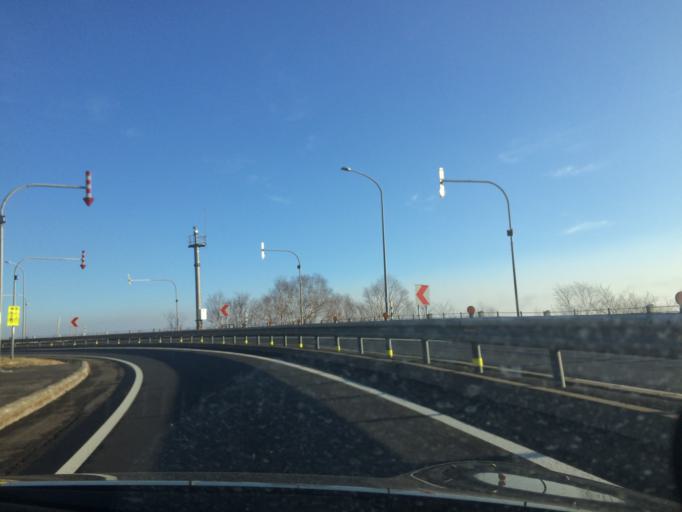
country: JP
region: Hokkaido
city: Otofuke
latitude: 42.9690
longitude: 142.7983
